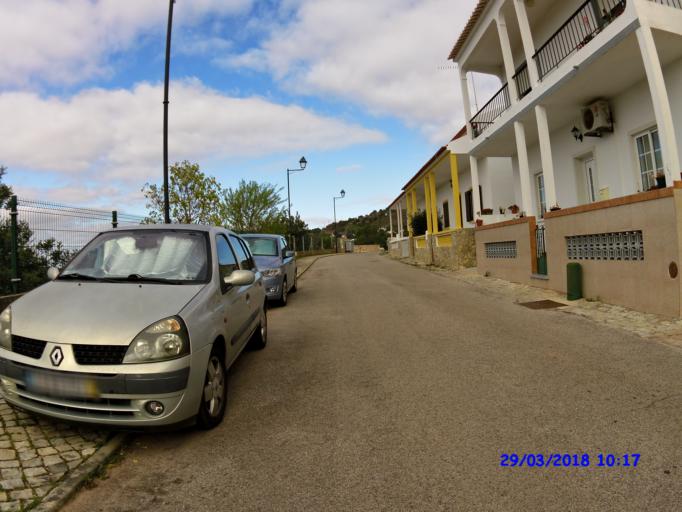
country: PT
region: Faro
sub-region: Loule
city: Boliqueime
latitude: 37.2347
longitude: -8.1706
